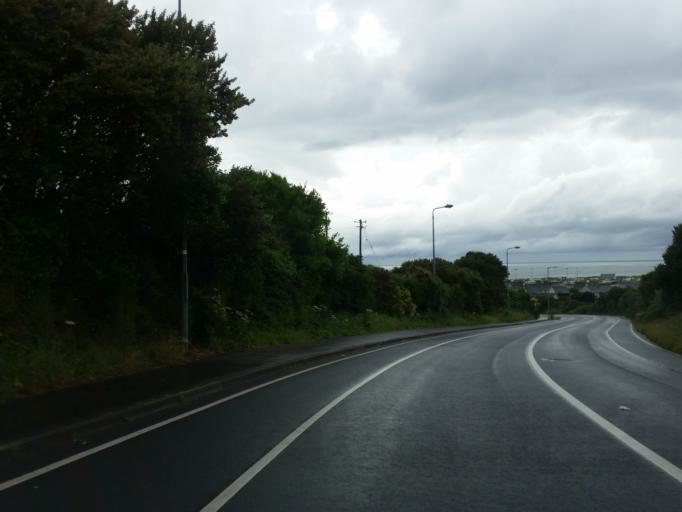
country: IE
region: Connaught
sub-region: Sligo
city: Strandhill
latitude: 54.2696
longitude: -8.5945
